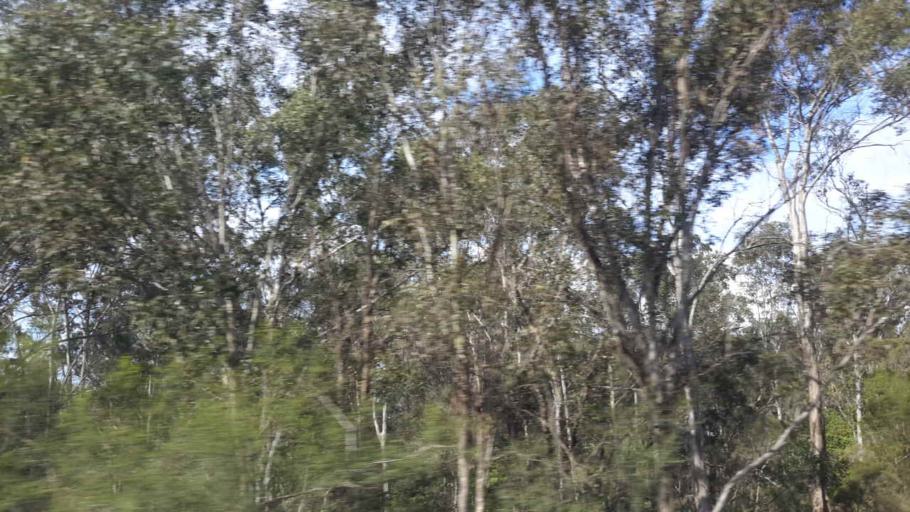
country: AU
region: New South Wales
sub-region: Hawkesbury
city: South Windsor
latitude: -33.6322
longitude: 150.7779
